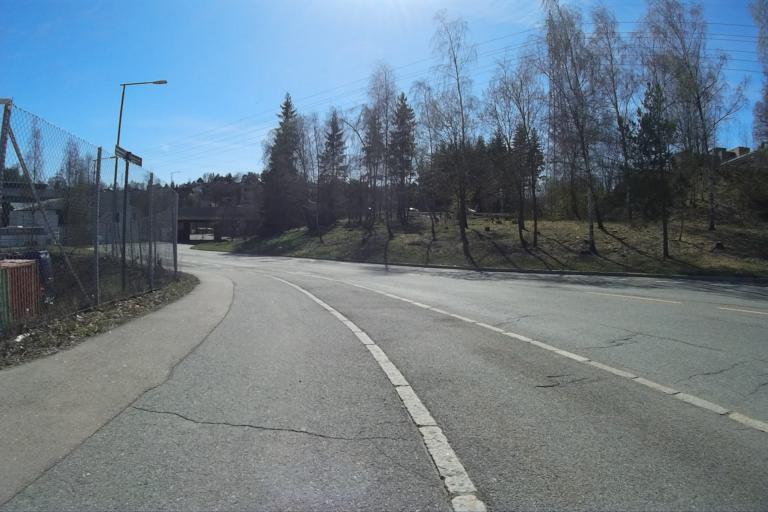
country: NO
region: Oslo
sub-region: Oslo
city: Oslo
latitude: 59.9102
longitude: 10.8202
